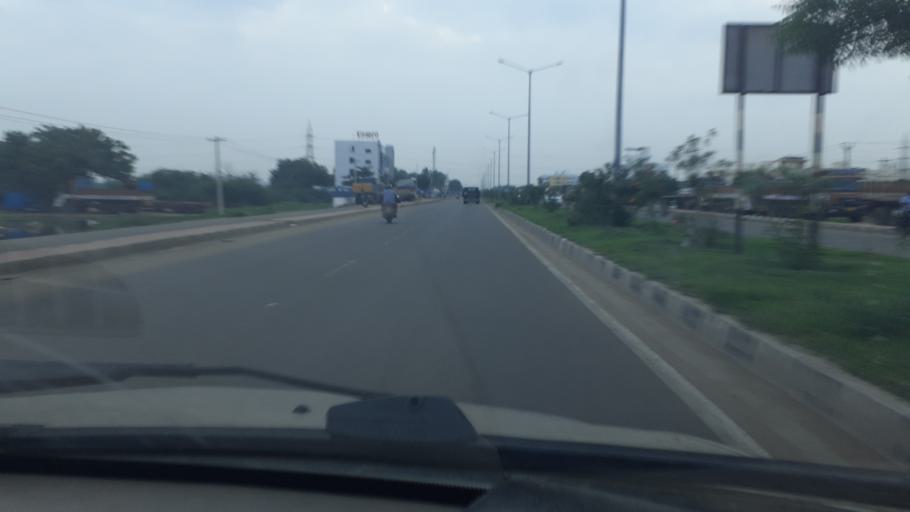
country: IN
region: Tamil Nadu
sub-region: Thoothukkudi
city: Korampallam
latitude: 8.7845
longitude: 78.1051
